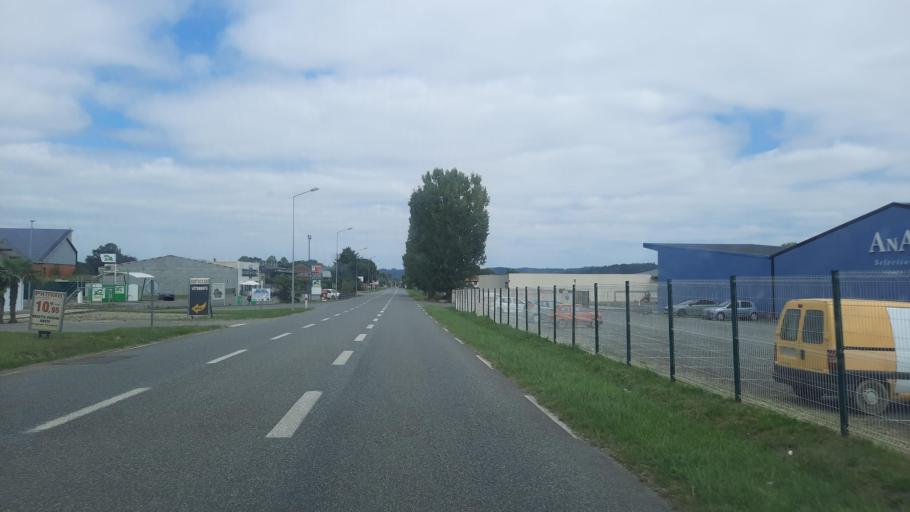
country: FR
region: Midi-Pyrenees
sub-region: Departement des Hautes-Pyrenees
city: Trie-sur-Baise
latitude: 43.3120
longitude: 0.3605
